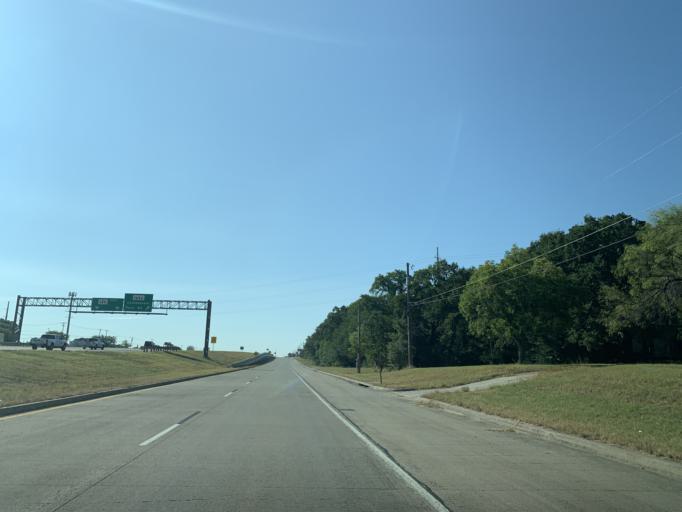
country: US
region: Texas
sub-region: Tarrant County
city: Lakeside
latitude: 32.8318
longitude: -97.4859
